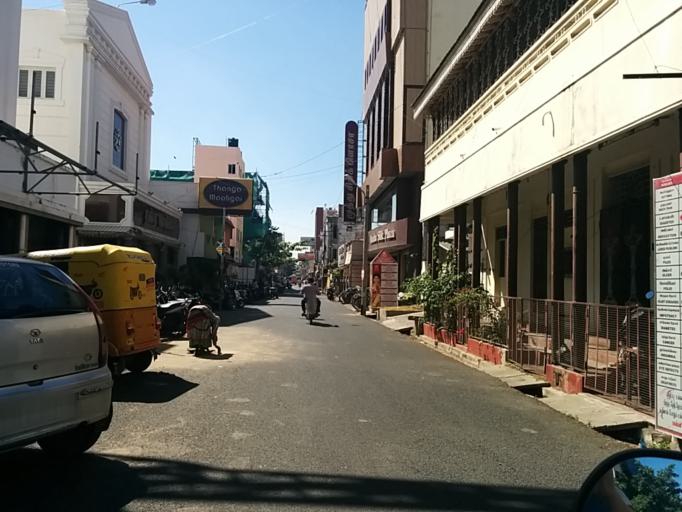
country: IN
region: Pondicherry
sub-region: Puducherry
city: Puducherry
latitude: 11.9367
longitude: 79.8300
